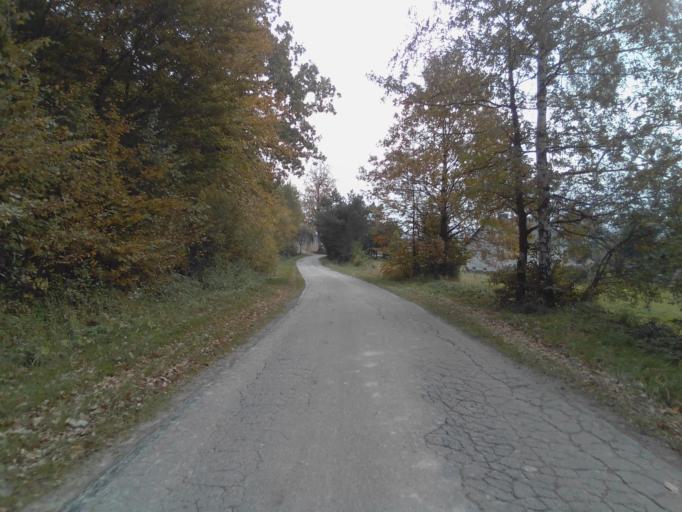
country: PL
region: Subcarpathian Voivodeship
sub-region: Powiat rzeszowski
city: Straszydle
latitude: 49.8608
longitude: 21.9746
